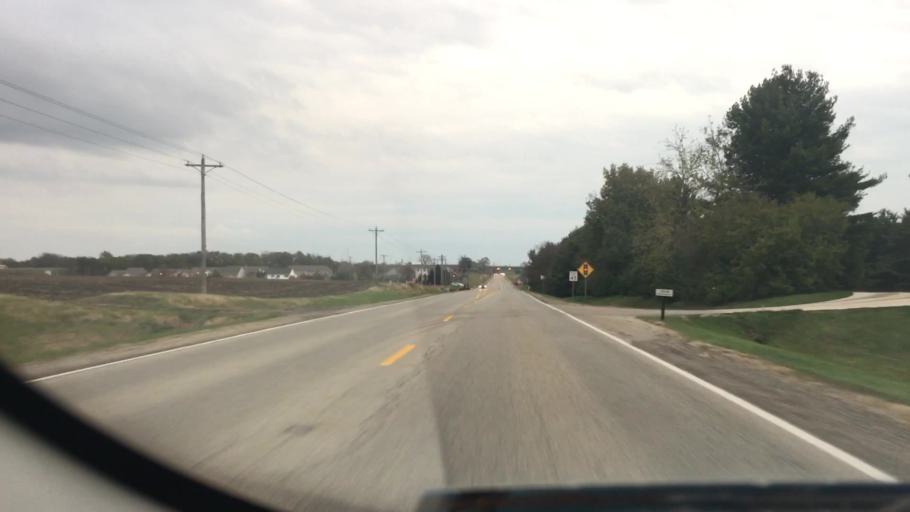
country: US
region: Illinois
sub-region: McLean County
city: Normal
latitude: 40.5118
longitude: -89.0366
